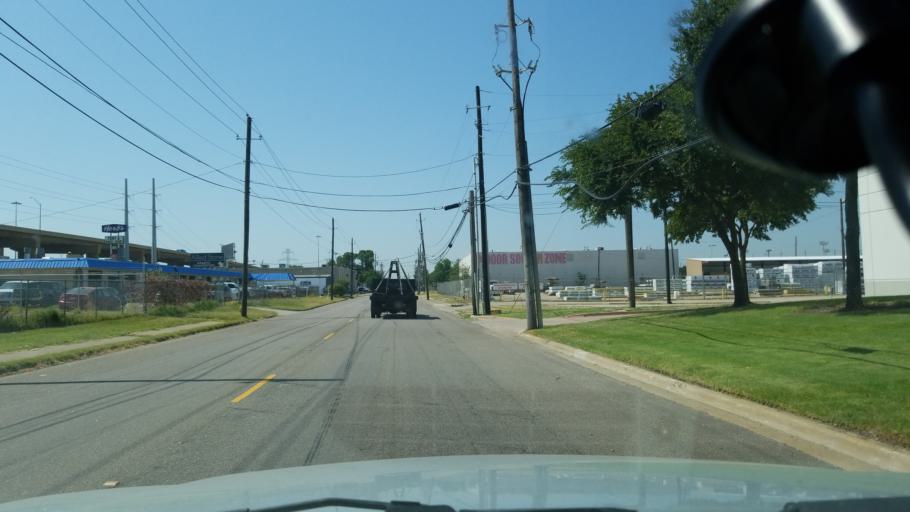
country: US
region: Texas
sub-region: Dallas County
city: Farmers Branch
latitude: 32.9027
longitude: -96.8995
